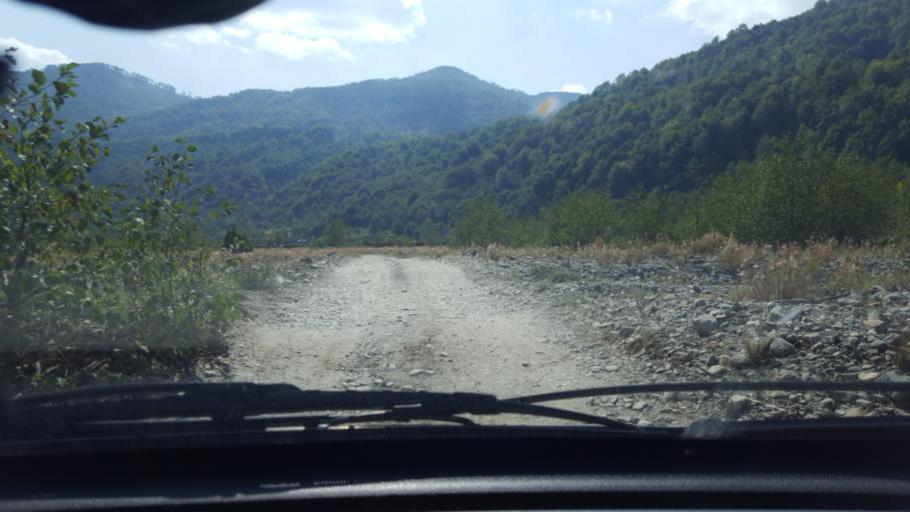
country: ME
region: Andrijevica
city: Andrijevica
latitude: 42.5964
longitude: 19.6734
